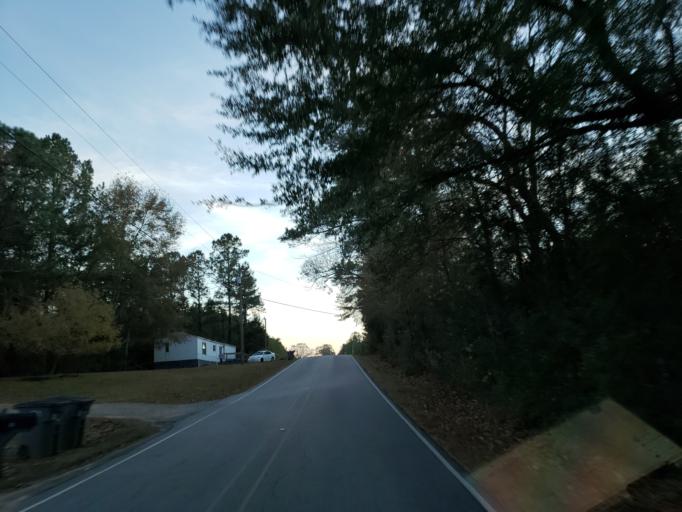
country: US
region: Mississippi
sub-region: Forrest County
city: Hattiesburg
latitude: 31.2526
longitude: -89.3141
